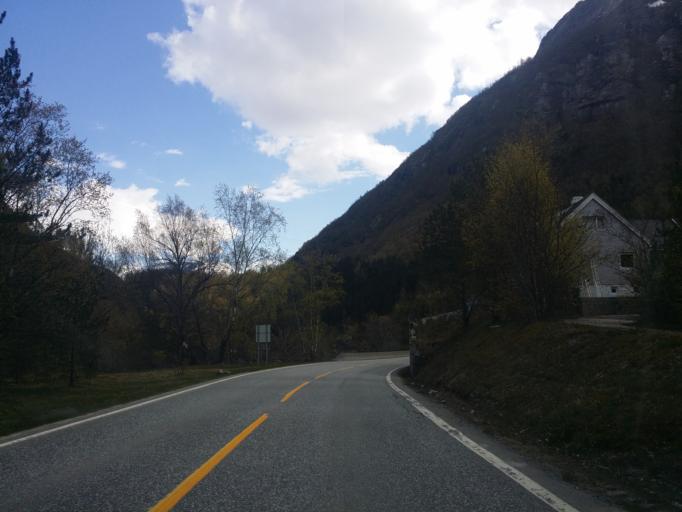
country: NO
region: Hordaland
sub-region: Eidfjord
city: Eidfjord
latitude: 60.4601
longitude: 7.0808
